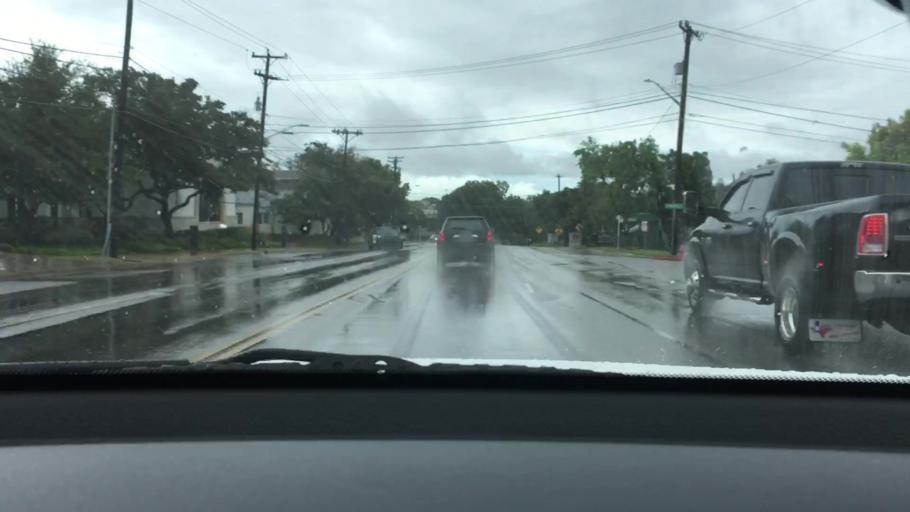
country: US
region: Texas
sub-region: Bexar County
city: Alamo Heights
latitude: 29.4848
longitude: -98.4665
